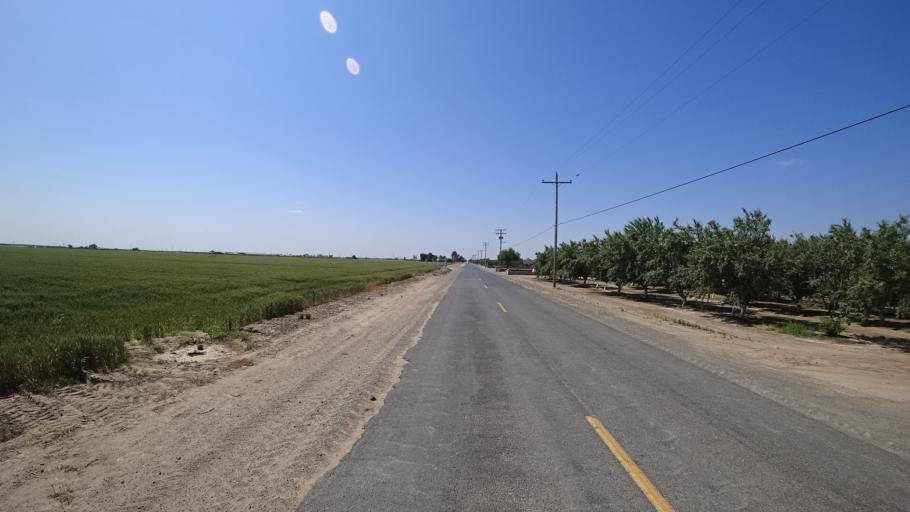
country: US
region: California
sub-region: Kings County
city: Home Garden
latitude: 36.2922
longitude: -119.6190
